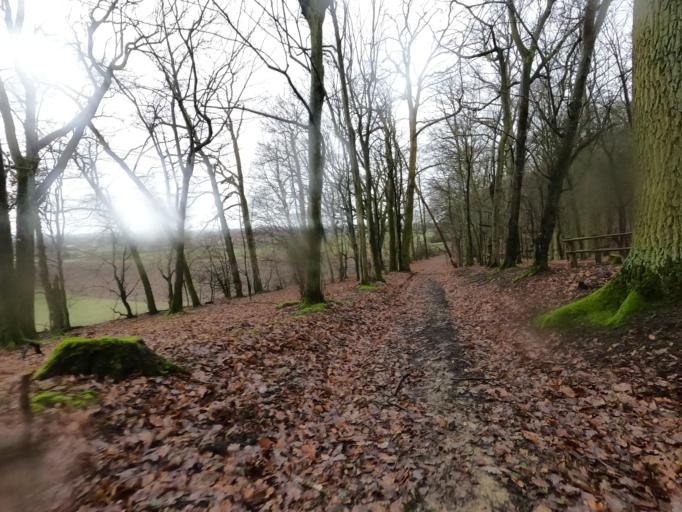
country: PL
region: Greater Poland Voivodeship
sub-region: Powiat pilski
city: Osiek nad Notecia
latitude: 53.1178
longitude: 17.2620
